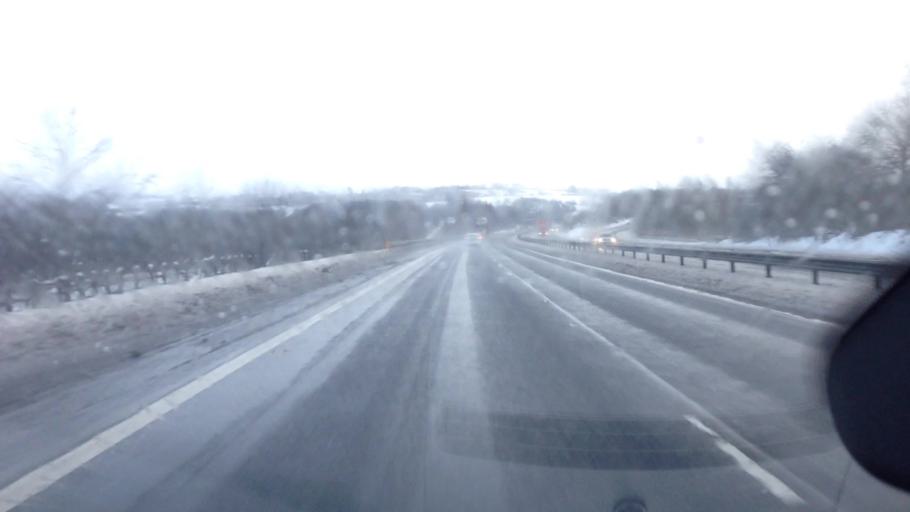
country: GB
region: Scotland
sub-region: South Lanarkshire
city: Lesmahagow
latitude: 55.6542
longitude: -3.8985
